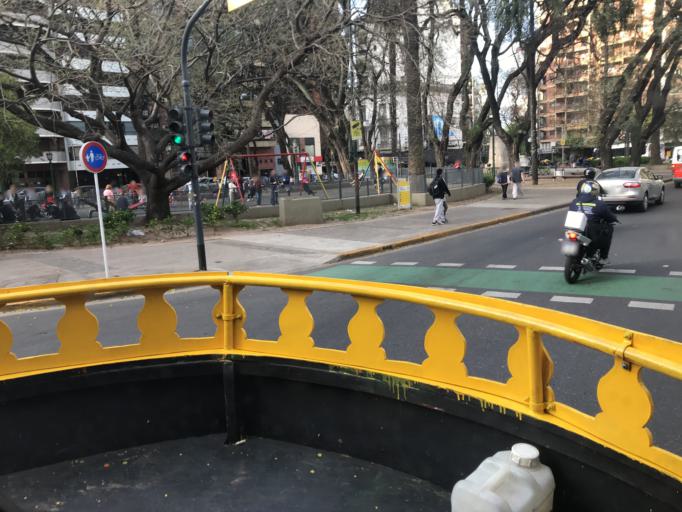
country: AR
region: Buenos Aires F.D.
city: Retiro
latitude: -34.5899
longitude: -58.4166
